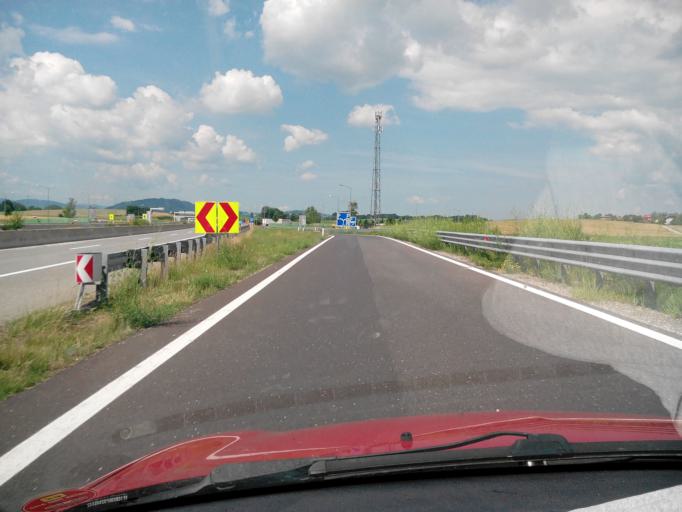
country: AT
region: Upper Austria
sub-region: Politischer Bezirk Vocklabruck
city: Aurach am Hongar
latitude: 47.9569
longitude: 13.6458
